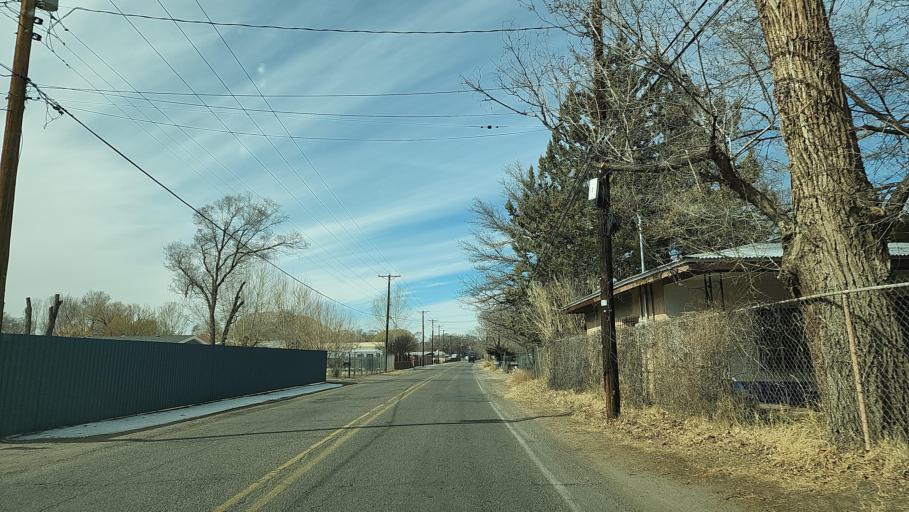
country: US
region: New Mexico
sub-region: Bernalillo County
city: South Valley
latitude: 35.0363
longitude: -106.6933
